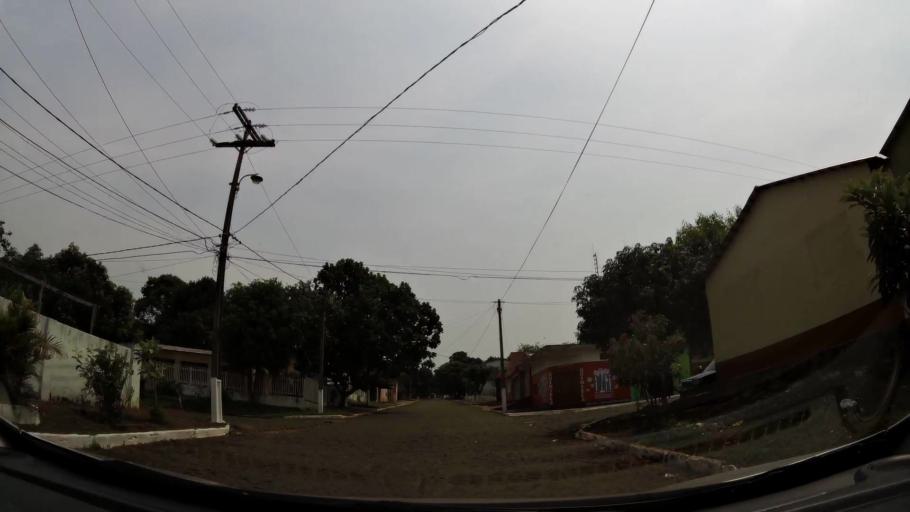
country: BR
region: Parana
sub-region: Foz Do Iguacu
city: Foz do Iguacu
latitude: -25.5662
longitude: -54.6057
